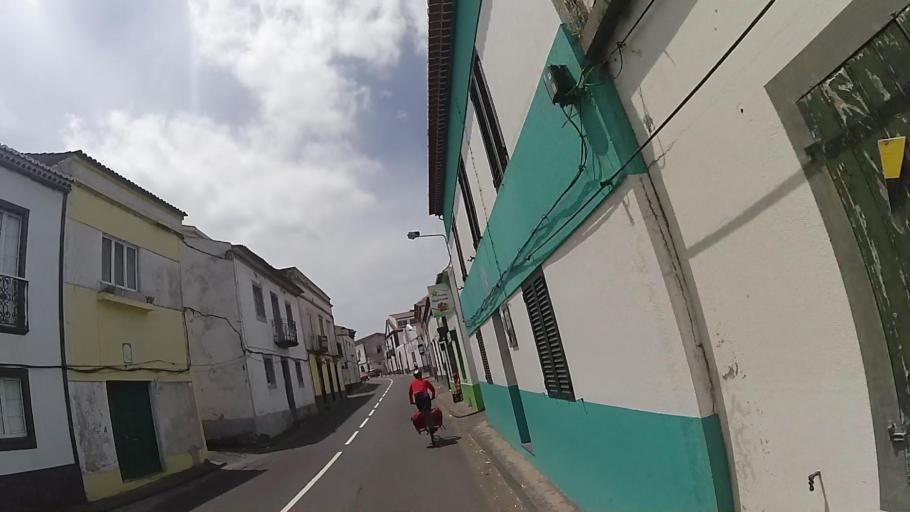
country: PT
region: Azores
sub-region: Ponta Delgada
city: Rosto de Cao
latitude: 37.7497
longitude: -25.6325
